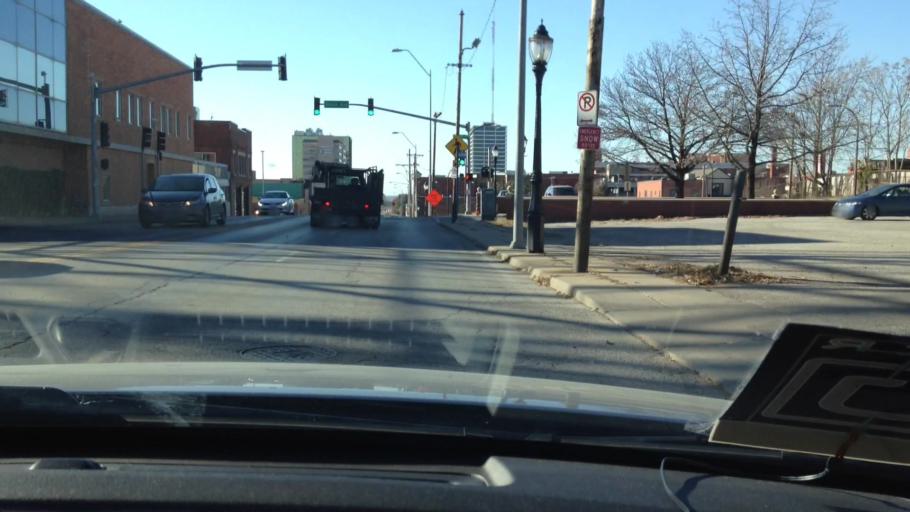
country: US
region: Missouri
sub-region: Jackson County
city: Kansas City
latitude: 39.0710
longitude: -94.5824
